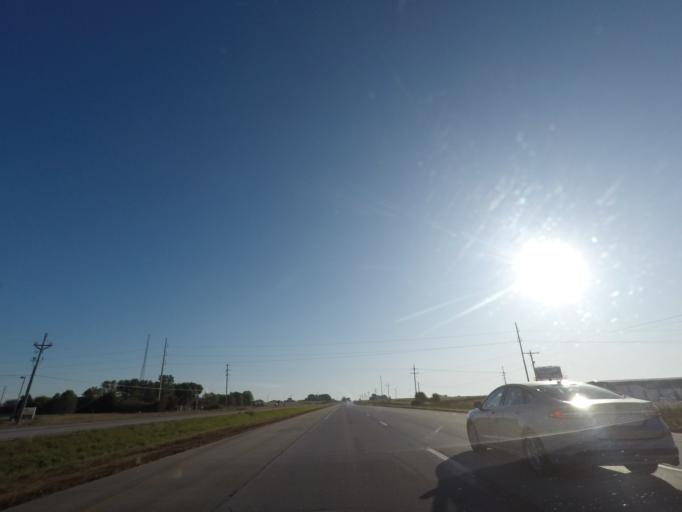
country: US
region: Iowa
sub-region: Story County
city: Ames
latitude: 42.0082
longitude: -93.5624
